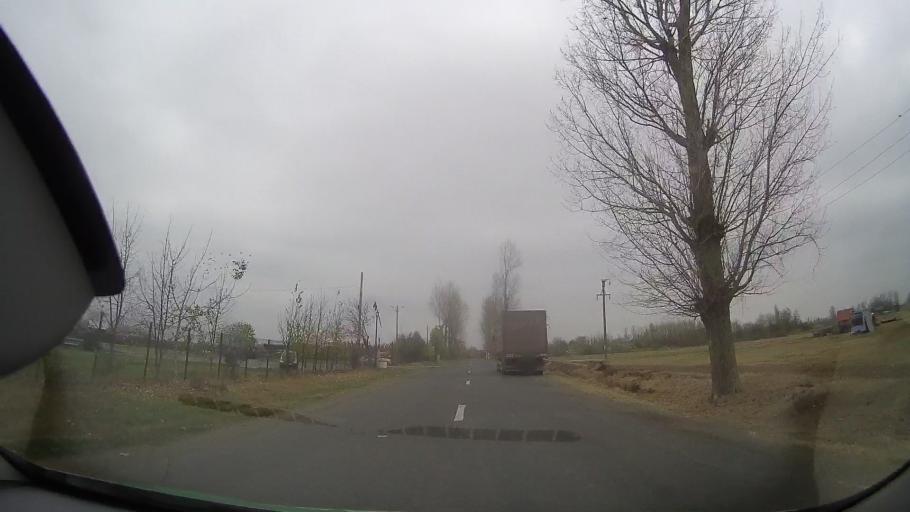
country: RO
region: Ialomita
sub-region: Comuna Grindu
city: Grindu
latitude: 44.7818
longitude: 26.9055
